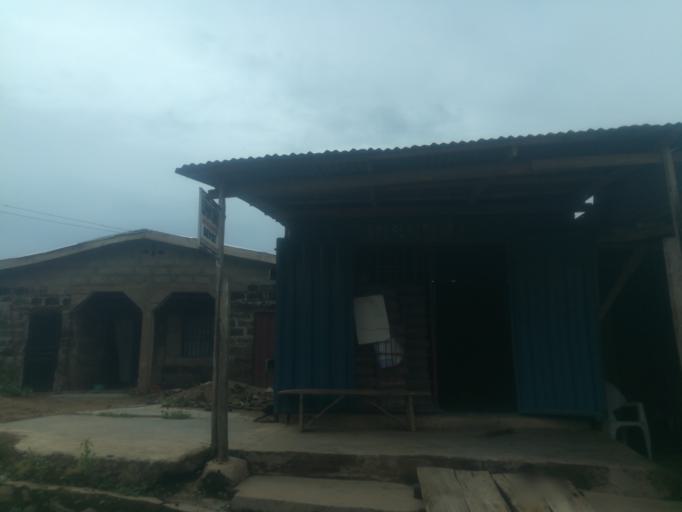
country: NG
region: Oyo
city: Ibadan
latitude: 7.3367
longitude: 3.9081
